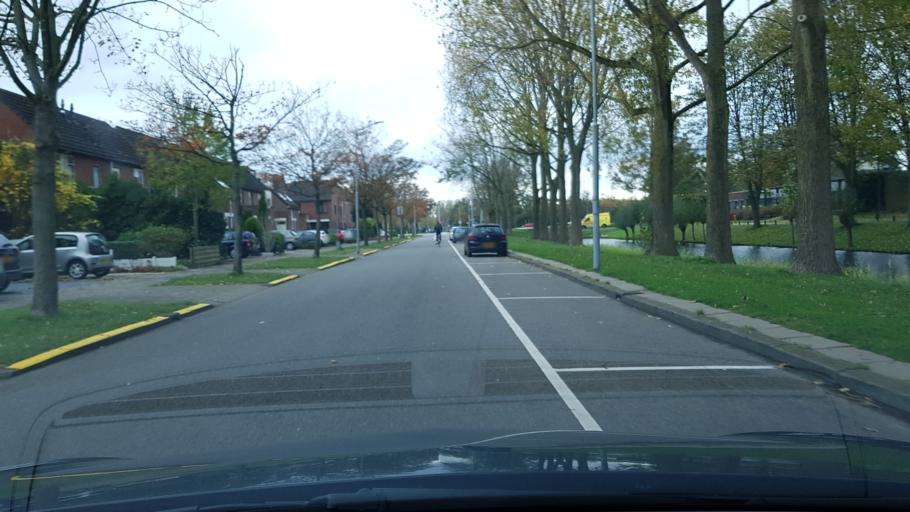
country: NL
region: North Holland
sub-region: Gemeente Haarlemmermeer
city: Hoofddorp
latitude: 52.3116
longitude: 4.6751
